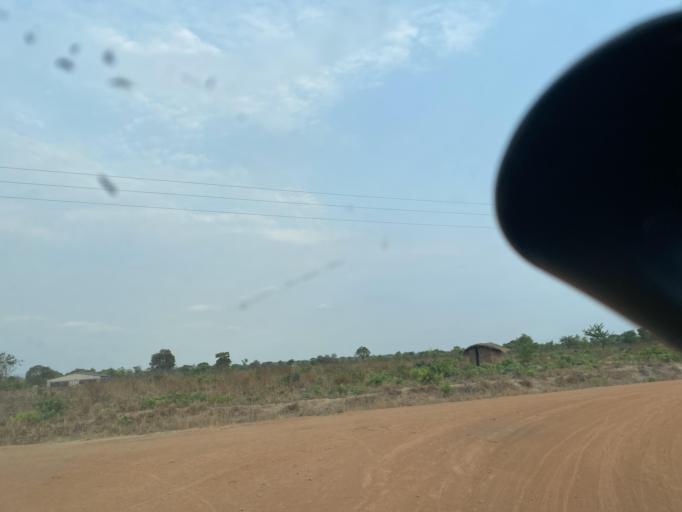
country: ZM
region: Lusaka
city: Chongwe
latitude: -15.1945
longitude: 28.5817
